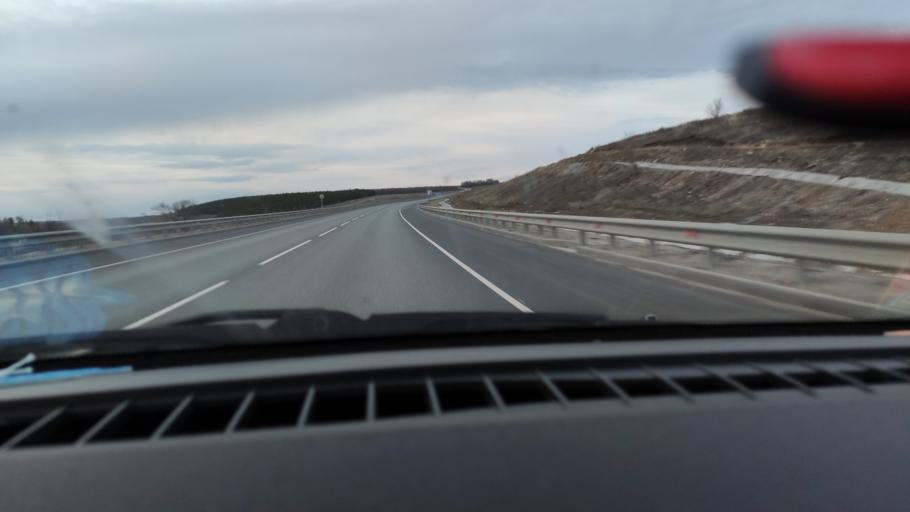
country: RU
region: Saratov
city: Yelshanka
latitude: 51.8758
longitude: 46.5063
